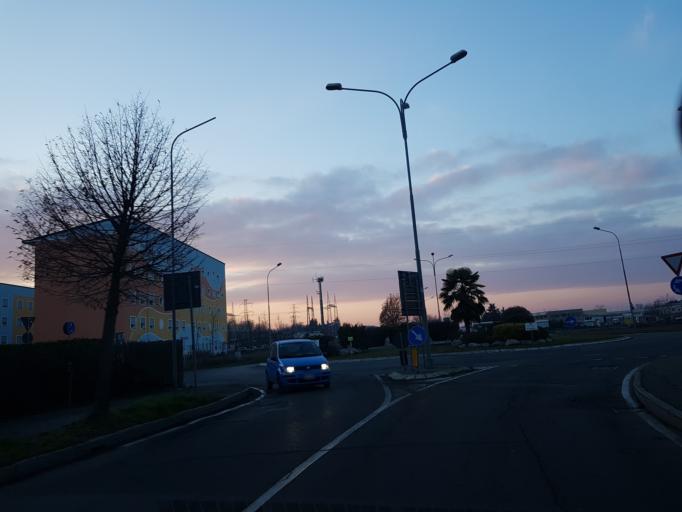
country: IT
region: Piedmont
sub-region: Provincia di Alessandria
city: Novi Ligure
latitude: 44.7659
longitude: 8.7710
